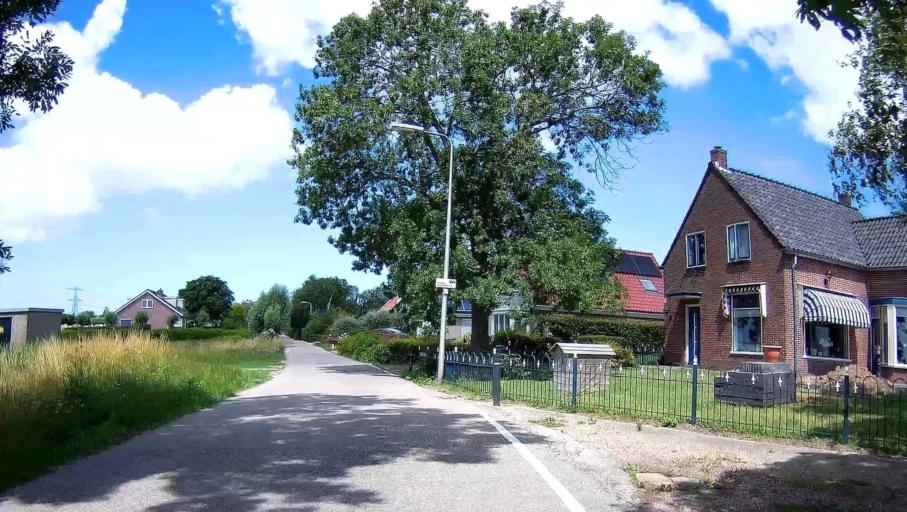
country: NL
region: South Holland
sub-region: Gemeente Westland
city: De Lier
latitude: 51.9839
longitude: 4.2473
